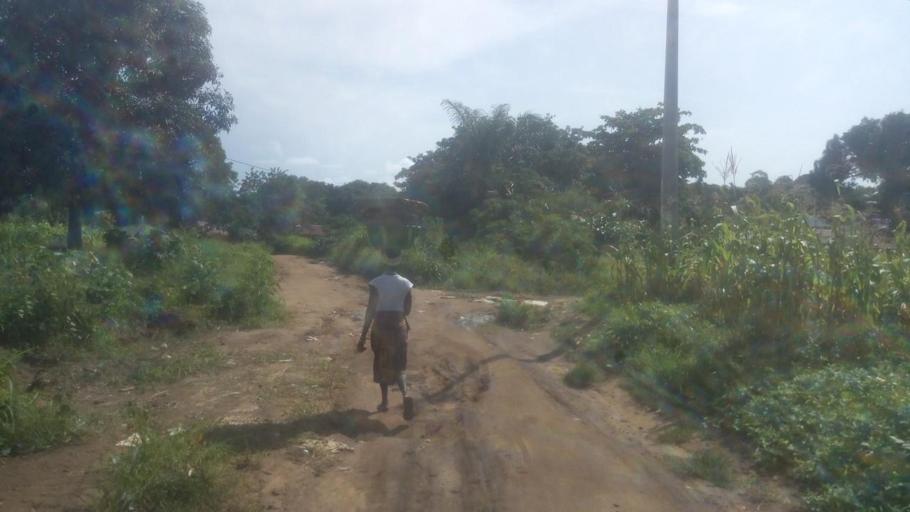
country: SL
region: Northern Province
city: Masoyila
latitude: 8.6085
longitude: -13.1991
